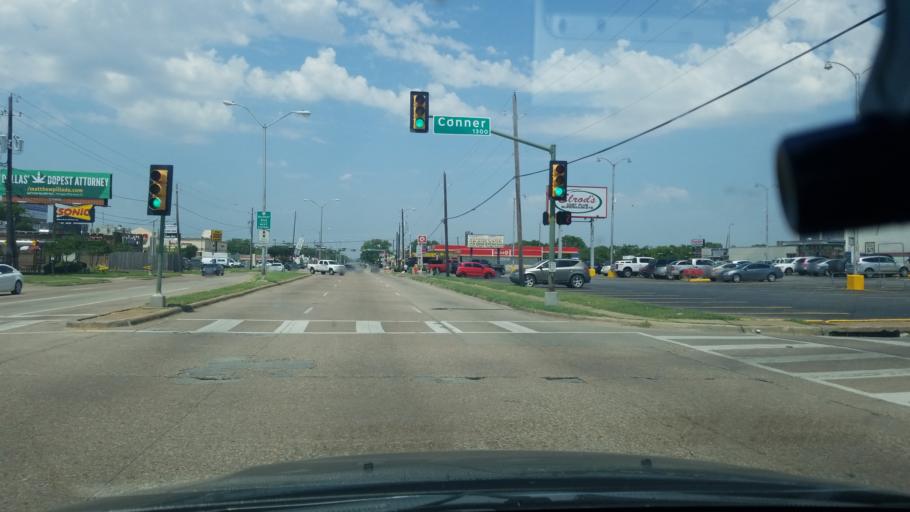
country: US
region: Texas
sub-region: Dallas County
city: Balch Springs
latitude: 32.7343
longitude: -96.6809
